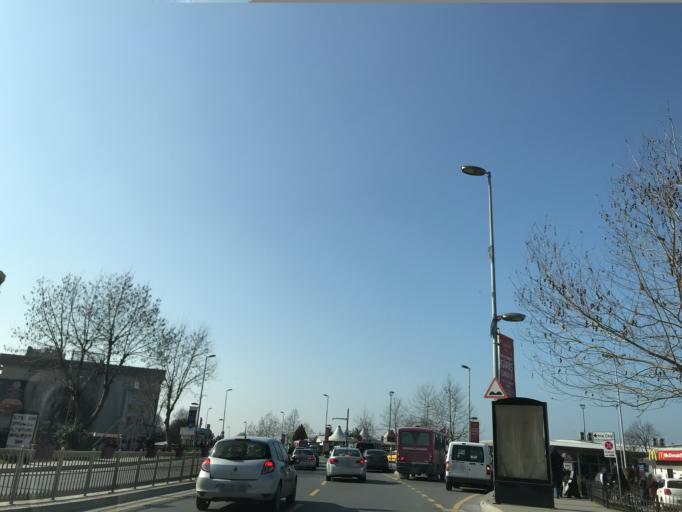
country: TR
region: Yalova
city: Yalova
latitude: 40.6590
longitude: 29.2799
